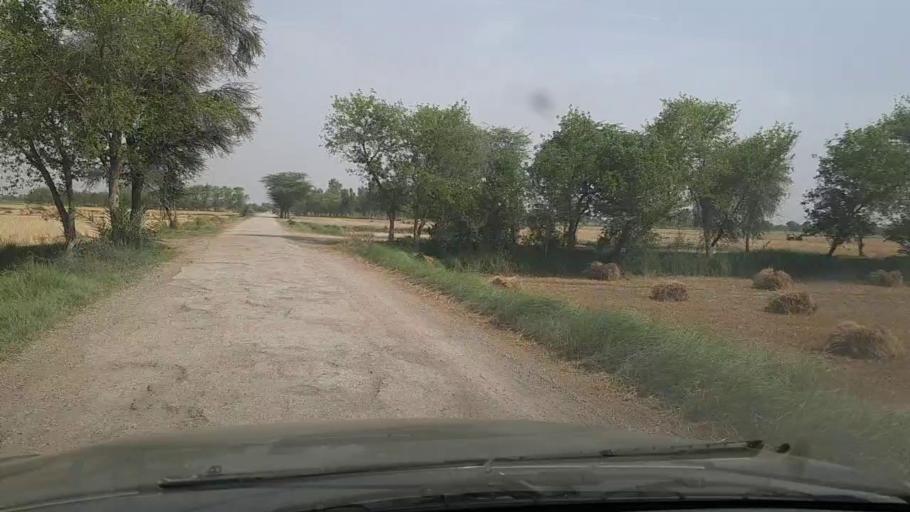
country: PK
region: Sindh
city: Lakhi
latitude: 27.8396
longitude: 68.7640
